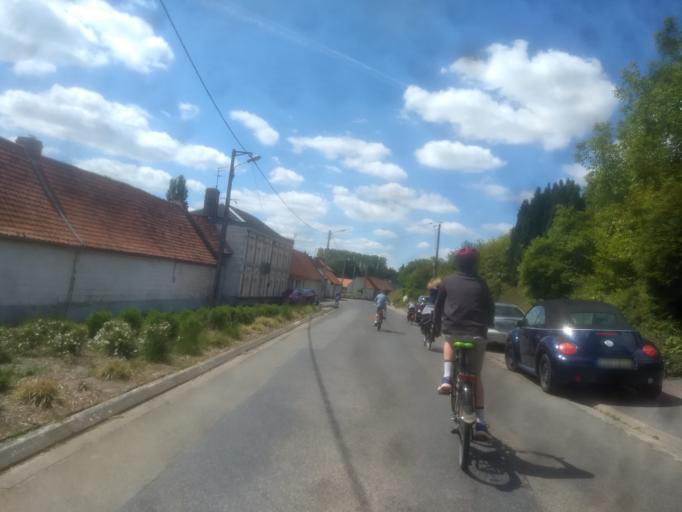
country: FR
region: Nord-Pas-de-Calais
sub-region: Departement du Pas-de-Calais
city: Riviere
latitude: 50.2322
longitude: 2.6832
